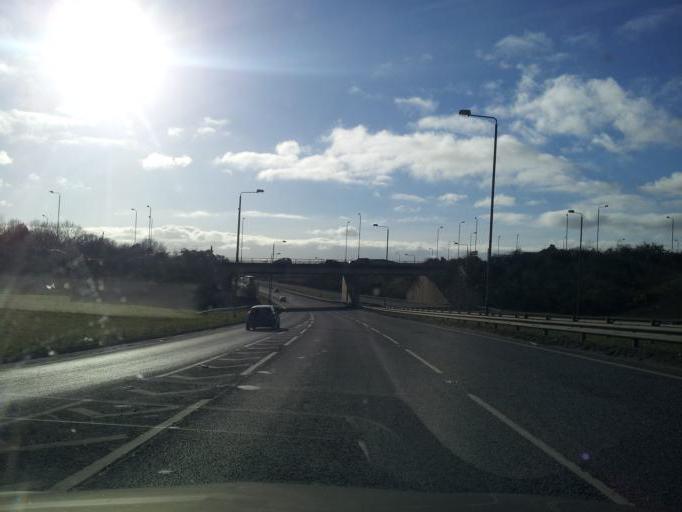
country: GB
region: England
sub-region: Derbyshire
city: Pinxton
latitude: 53.1093
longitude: -1.3134
